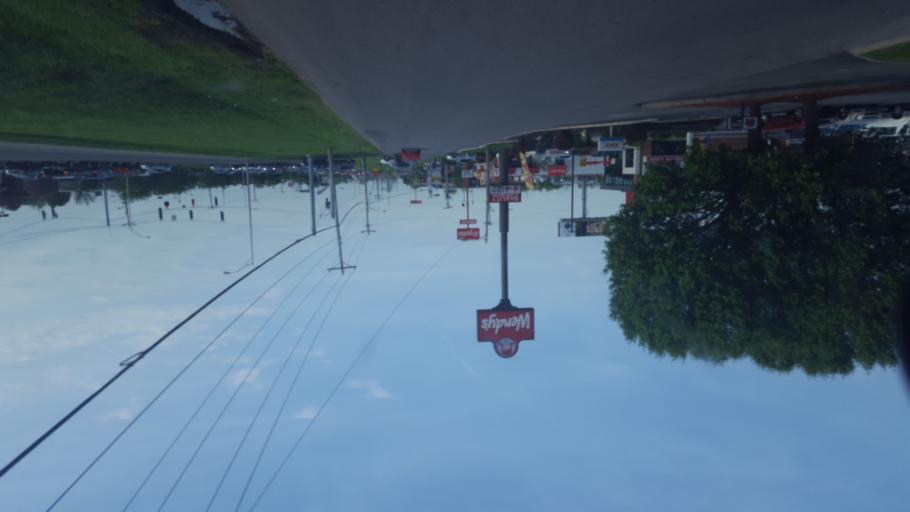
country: US
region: Kentucky
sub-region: Warren County
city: Bowling Green
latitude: 36.9497
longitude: -86.4245
